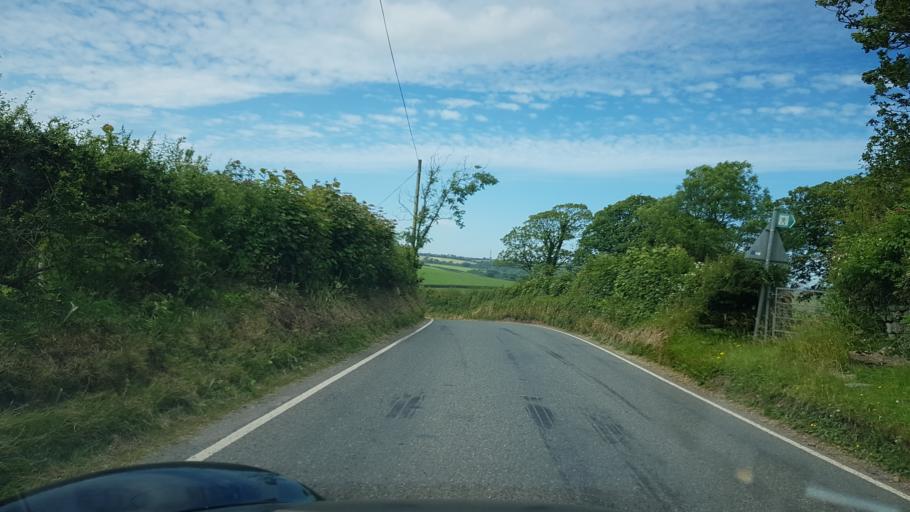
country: GB
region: Wales
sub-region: Carmarthenshire
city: Llanddowror
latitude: 51.7662
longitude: -4.5654
